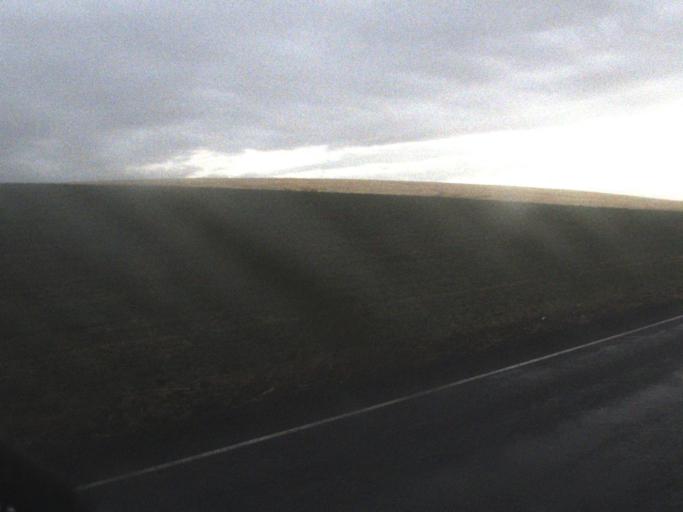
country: US
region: Washington
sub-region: Lincoln County
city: Davenport
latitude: 47.7150
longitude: -118.1515
